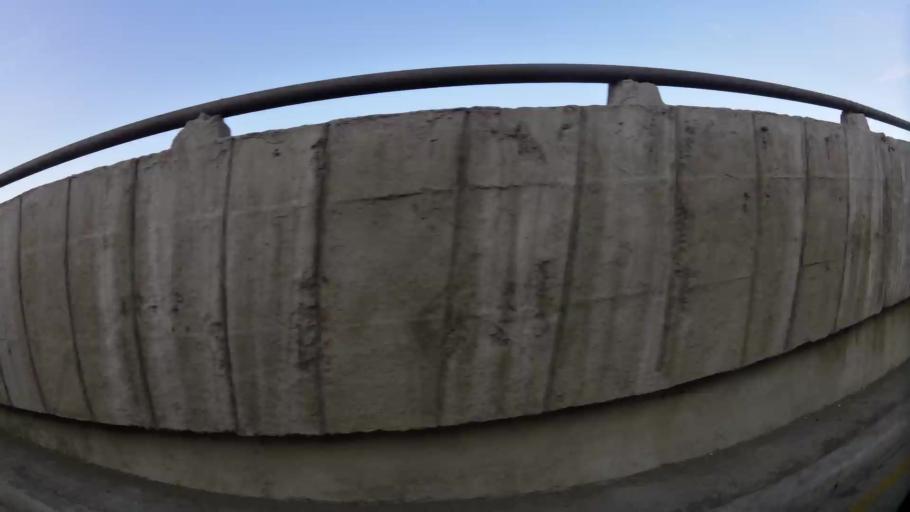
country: EC
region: Guayas
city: Guayaquil
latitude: -2.1805
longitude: -79.8923
